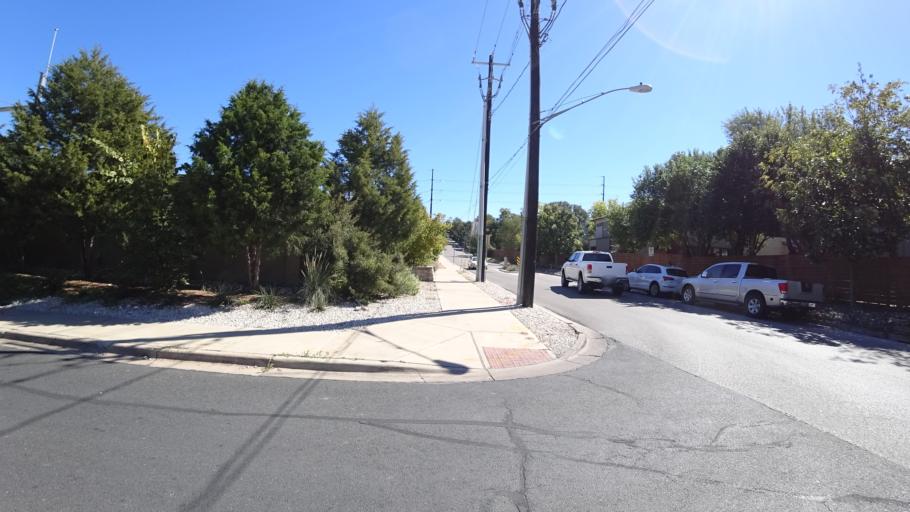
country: US
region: Texas
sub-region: Travis County
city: Austin
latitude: 30.2338
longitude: -97.7695
